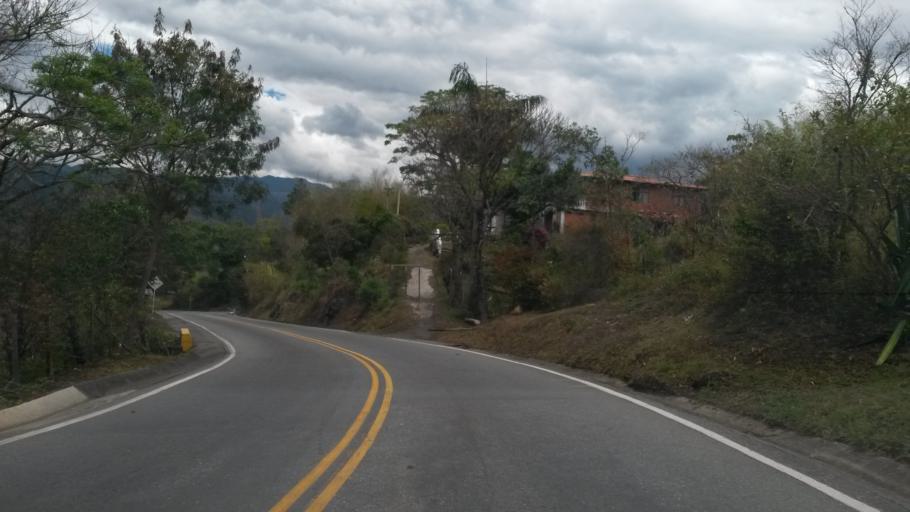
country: CO
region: Cauca
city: Rosas
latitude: 2.2745
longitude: -76.7205
